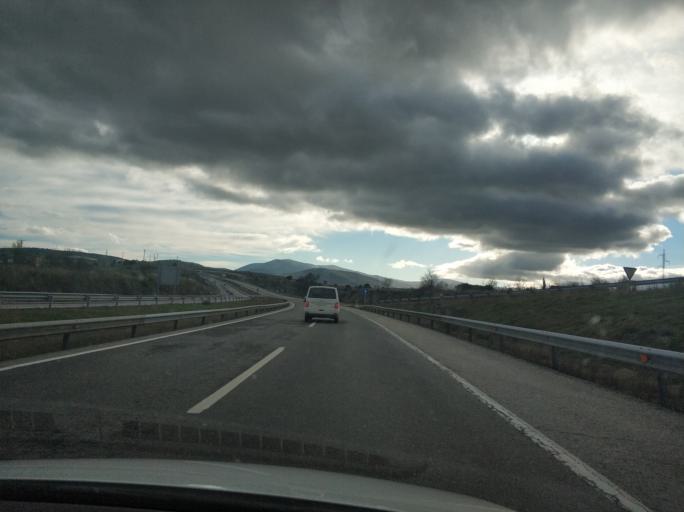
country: ES
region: Madrid
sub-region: Provincia de Madrid
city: Buitrago del Lozoya
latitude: 40.9977
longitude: -3.6413
